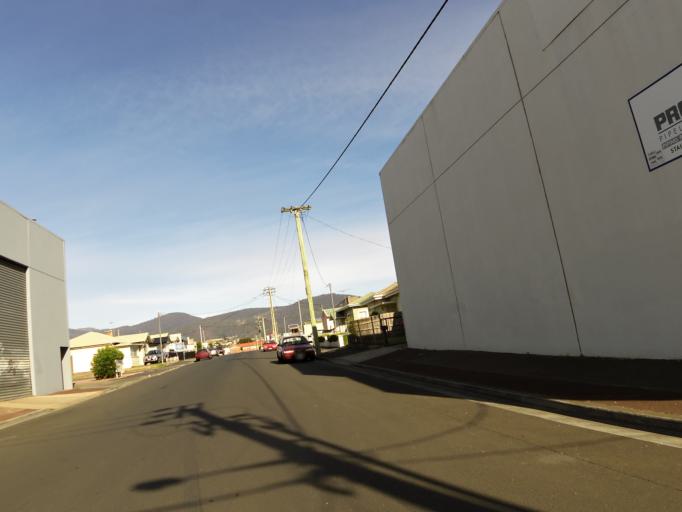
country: AU
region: Tasmania
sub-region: Glenorchy
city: Moonah
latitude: -42.8376
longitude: 147.3016
